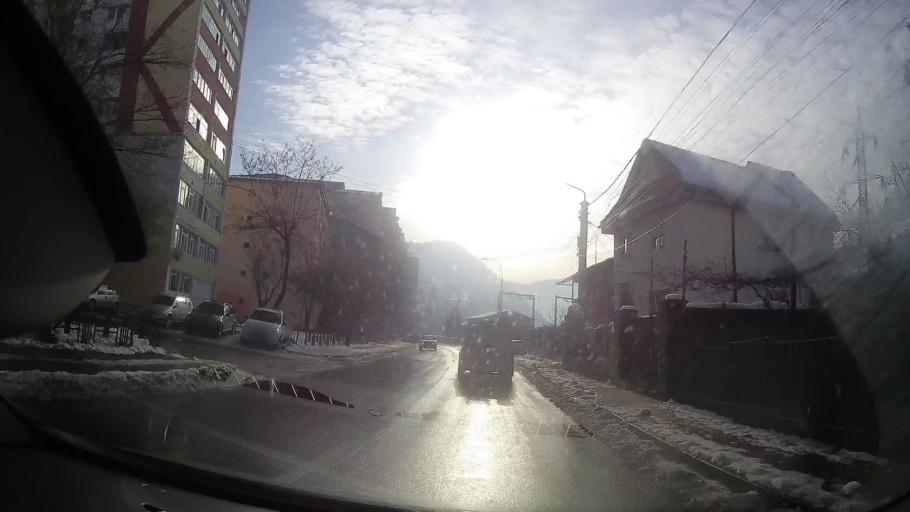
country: RO
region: Neamt
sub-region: Municipiul Piatra-Neamt
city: Valeni
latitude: 46.9396
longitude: 26.3815
